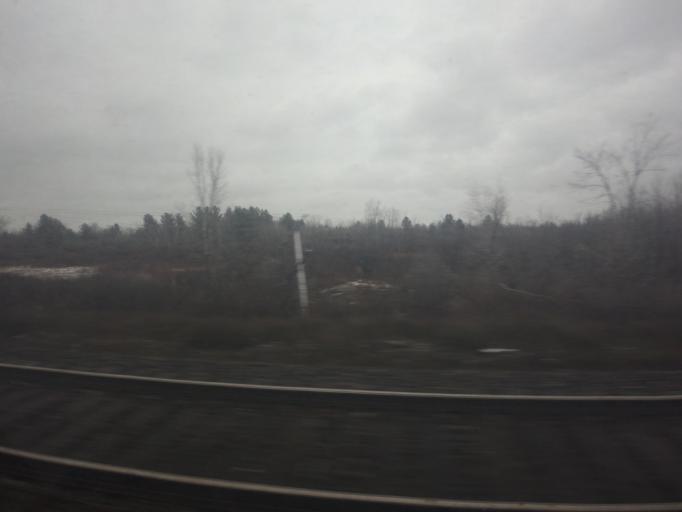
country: CA
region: Ontario
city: Gananoque
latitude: 44.3563
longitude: -76.2204
